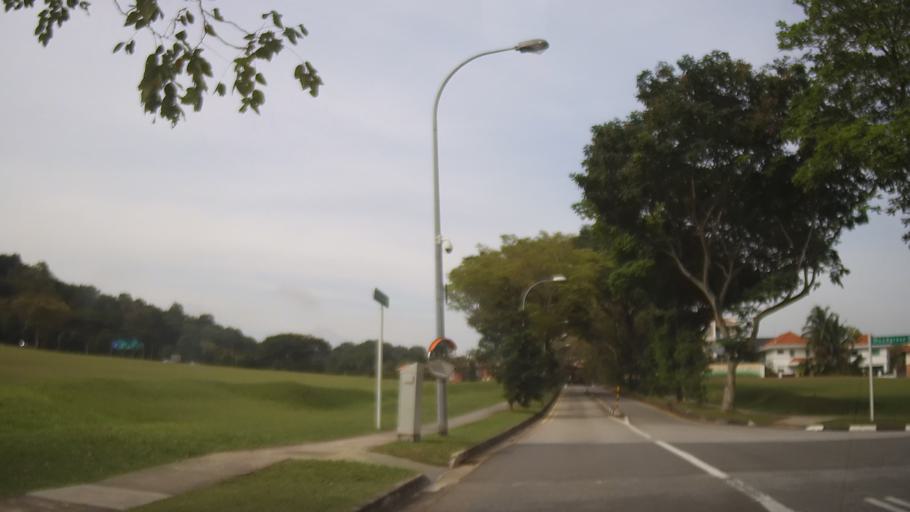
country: MY
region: Johor
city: Johor Bahru
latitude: 1.4285
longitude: 103.7823
